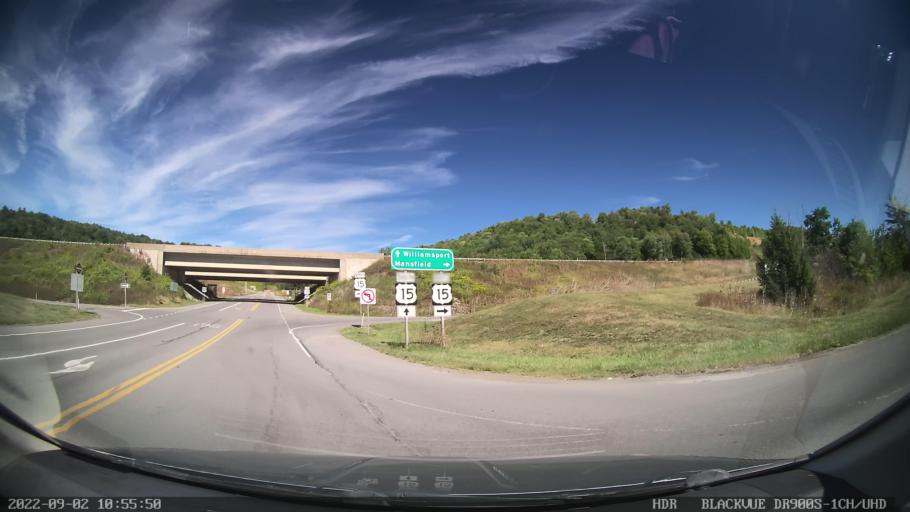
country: US
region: Pennsylvania
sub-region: Tioga County
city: Blossburg
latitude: 41.6723
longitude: -77.0751
